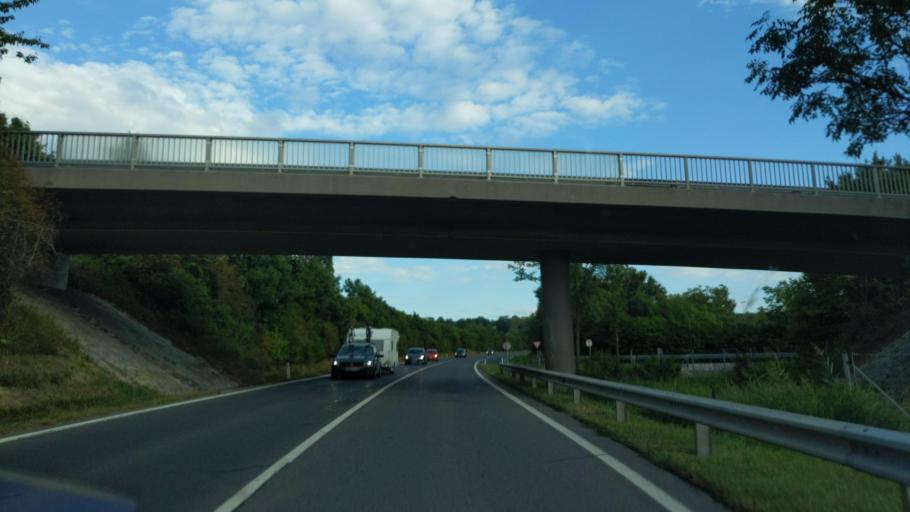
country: AT
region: Burgenland
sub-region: Eisenstadt-Umgebung
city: Klingenbach
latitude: 47.7609
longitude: 16.5418
